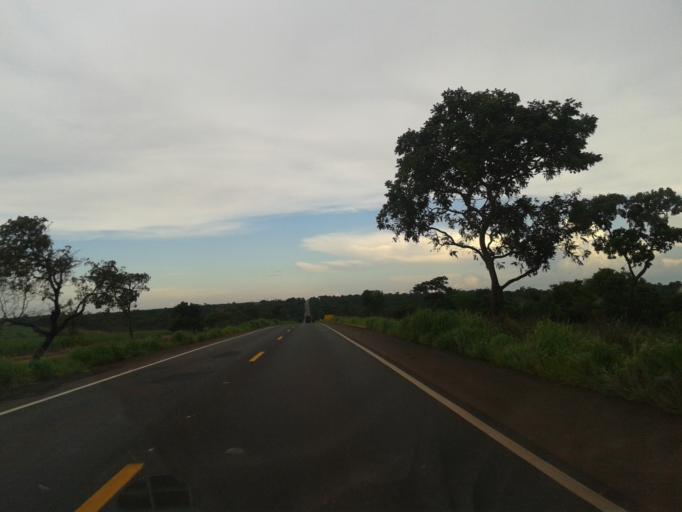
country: BR
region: Minas Gerais
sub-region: Santa Vitoria
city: Santa Vitoria
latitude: -18.8928
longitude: -50.1688
